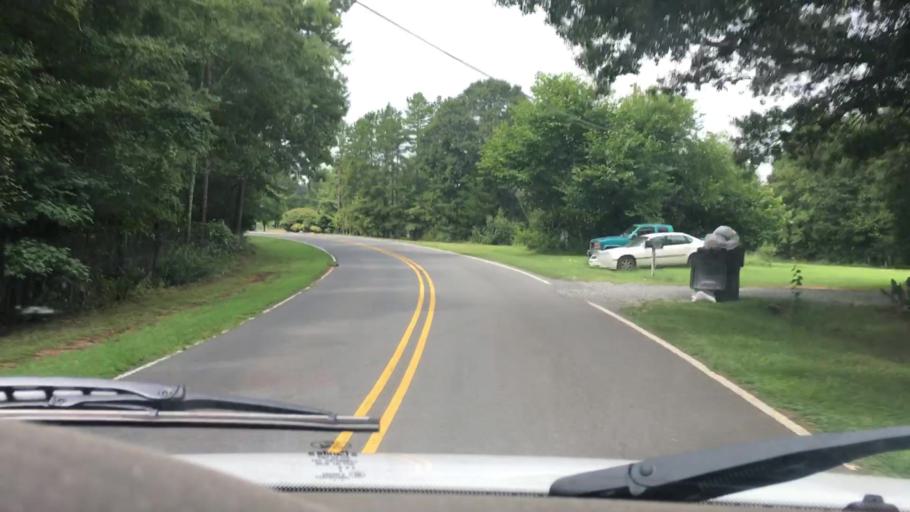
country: US
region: North Carolina
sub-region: Mecklenburg County
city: Cornelius
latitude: 35.4573
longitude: -80.8225
